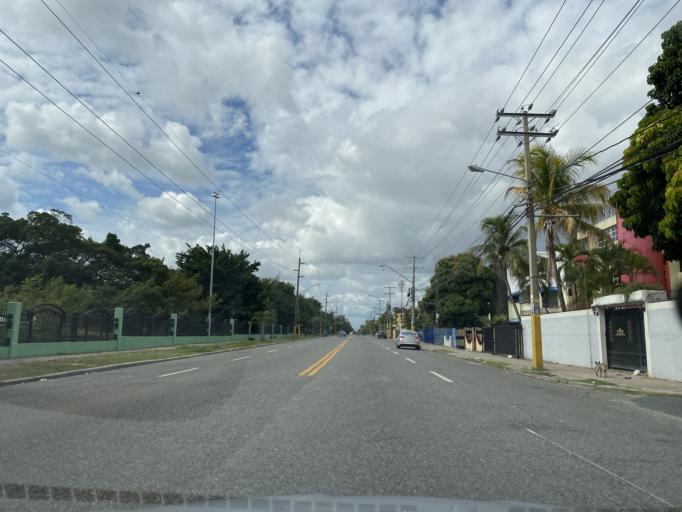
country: DO
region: Santo Domingo
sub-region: Santo Domingo
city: Santo Domingo Este
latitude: 18.4816
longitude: -69.8506
